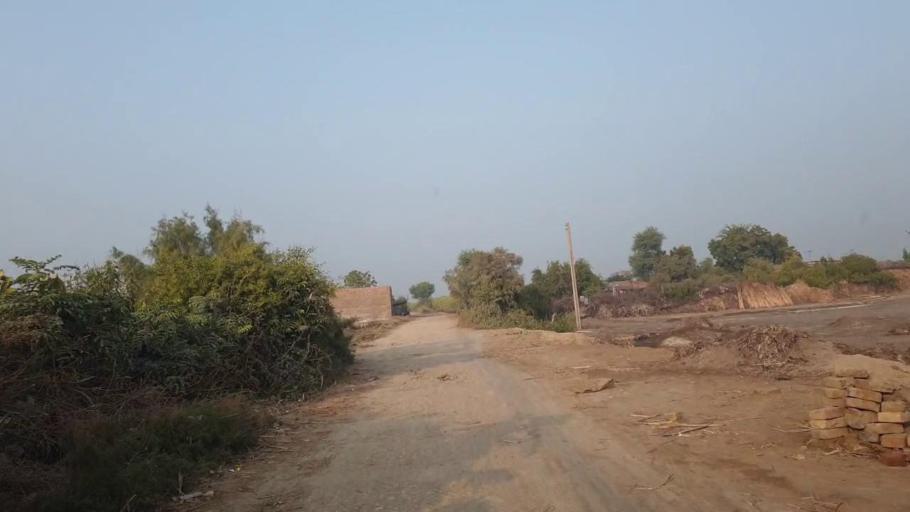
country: PK
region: Sindh
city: Shahdadpur
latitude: 25.8745
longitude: 68.6032
